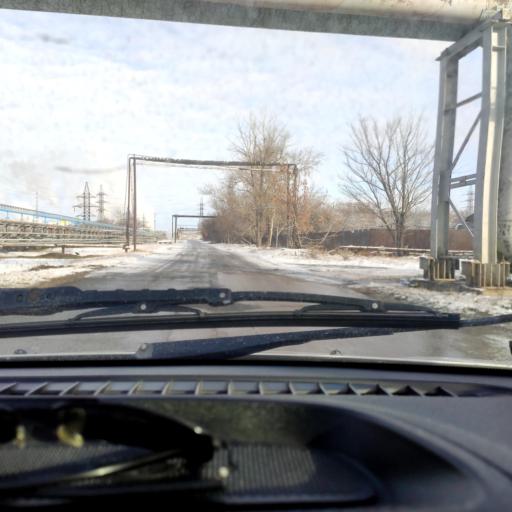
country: RU
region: Samara
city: Tol'yatti
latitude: 53.5377
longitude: 49.4836
